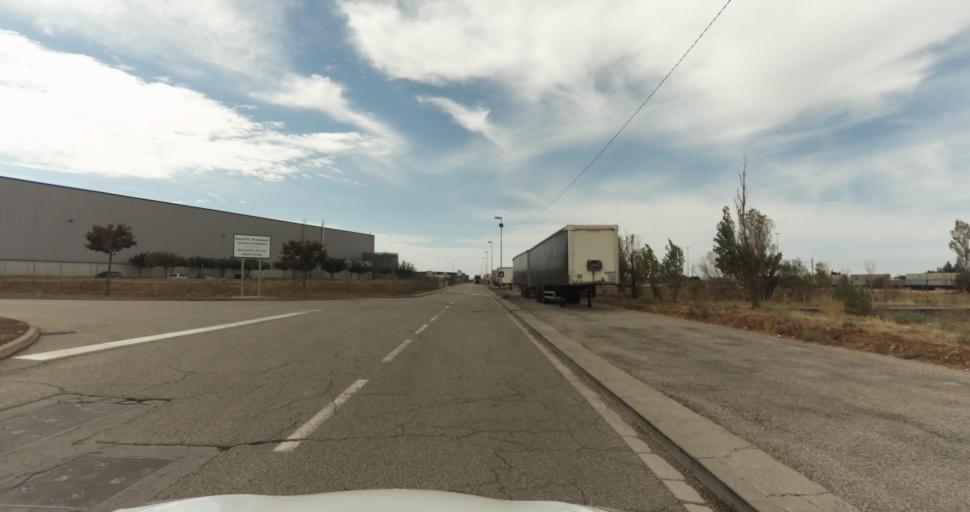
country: FR
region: Provence-Alpes-Cote d'Azur
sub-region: Departement des Bouches-du-Rhone
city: Miramas
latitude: 43.6106
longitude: 4.9943
